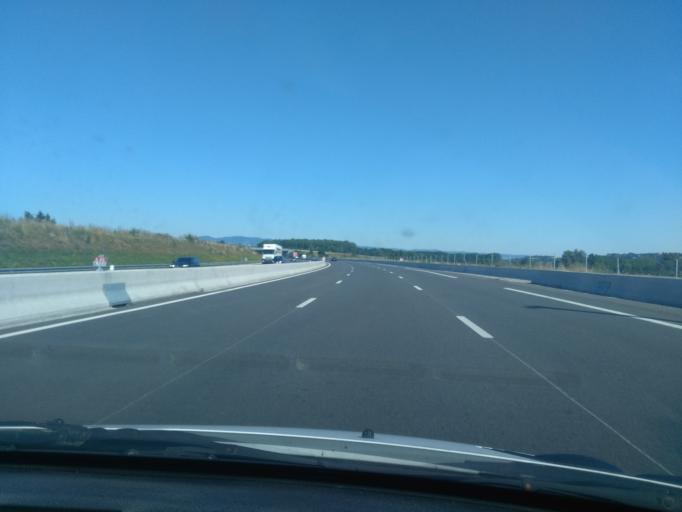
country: FR
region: Rhone-Alpes
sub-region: Departement du Rhone
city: Quincieux
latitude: 45.9151
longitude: 4.7920
